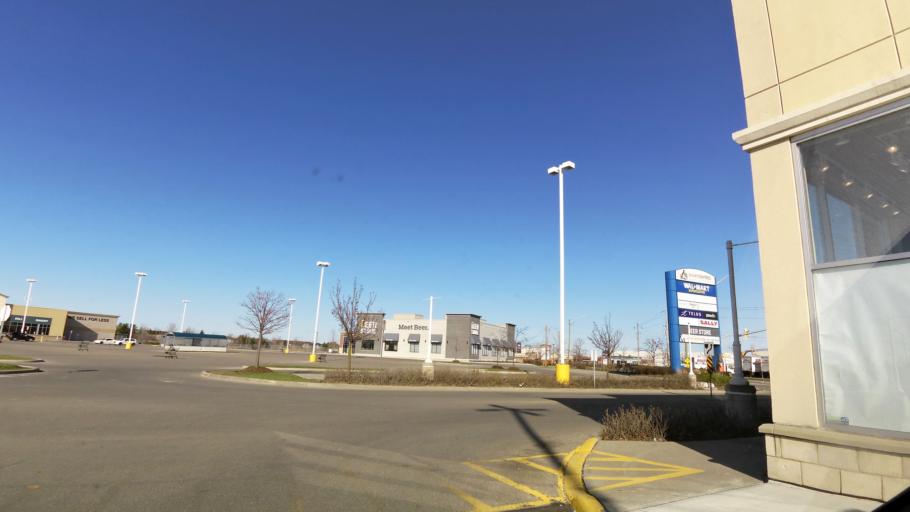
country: CA
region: Ontario
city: Brampton
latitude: 43.8631
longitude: -79.7118
